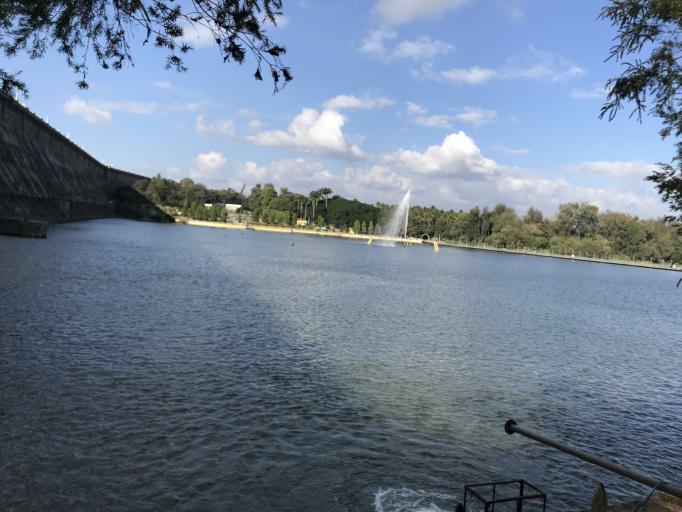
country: IN
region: Karnataka
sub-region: Mandya
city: Shrirangapattana
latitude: 12.4237
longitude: 76.5724
